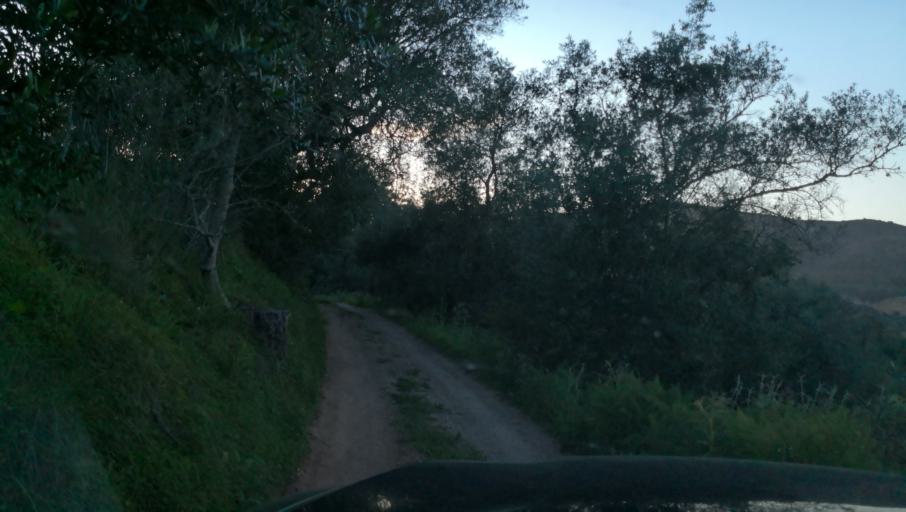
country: PT
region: Setubal
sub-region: Setubal
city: Setubal
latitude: 38.5208
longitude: -8.9225
